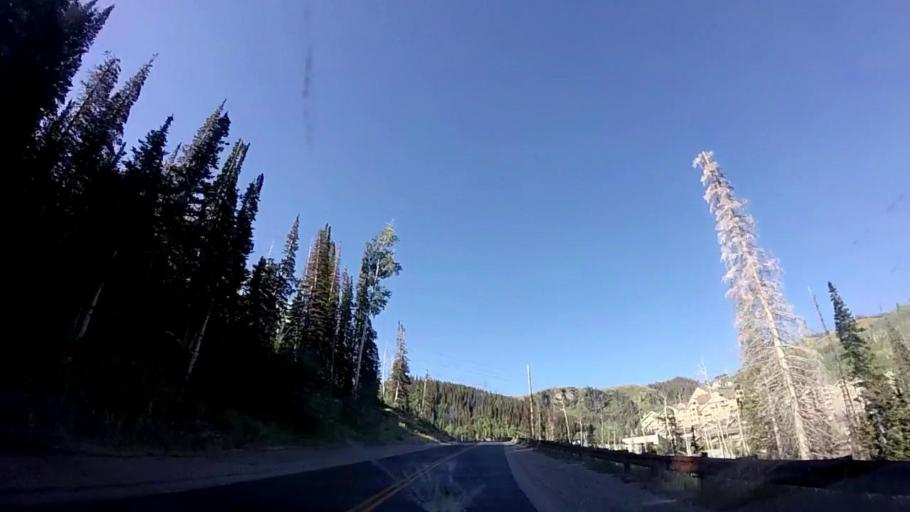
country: US
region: Utah
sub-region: Summit County
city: Park City
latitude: 40.6174
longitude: -111.5081
